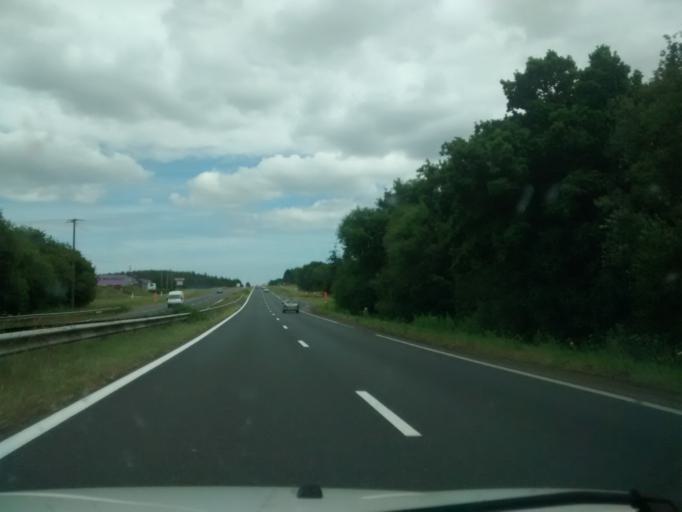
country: FR
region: Brittany
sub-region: Departement des Cotes-d'Armor
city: Saint-Agathon
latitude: 48.5426
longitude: -3.0794
